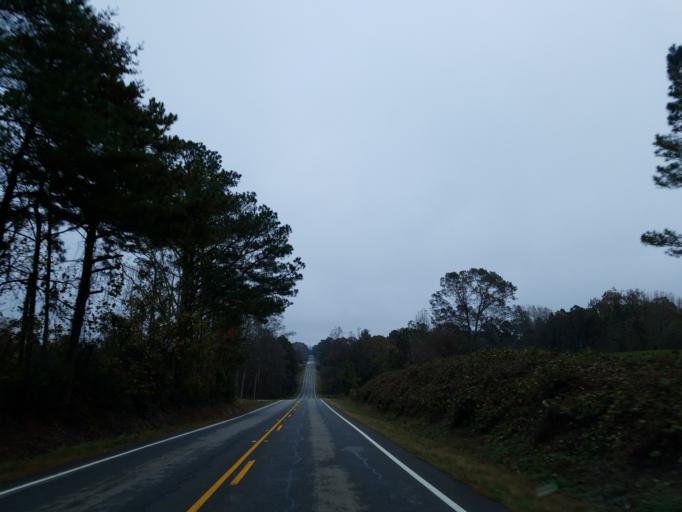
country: US
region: Georgia
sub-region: Pickens County
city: Jasper
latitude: 34.3920
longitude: -84.4595
